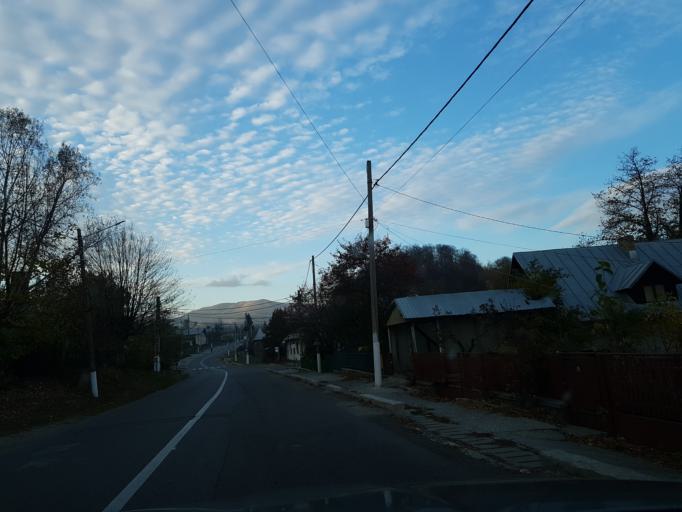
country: RO
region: Prahova
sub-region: Oras Breaza
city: Gura Beliei
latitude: 45.2095
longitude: 25.6478
